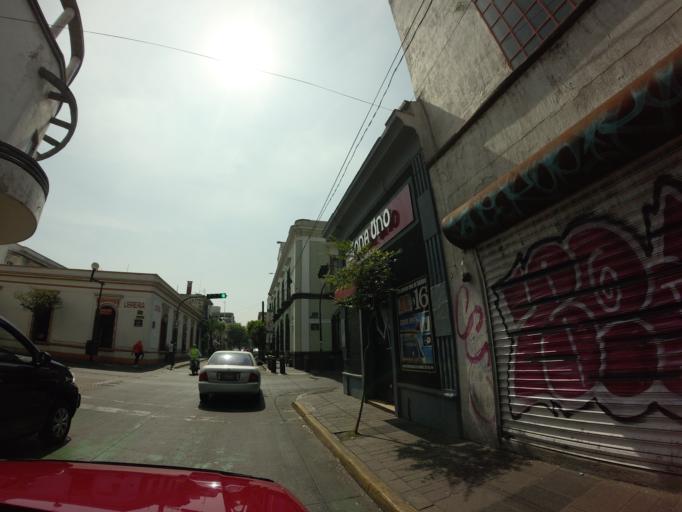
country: MX
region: Jalisco
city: Guadalajara
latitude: 20.6741
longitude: -103.3526
